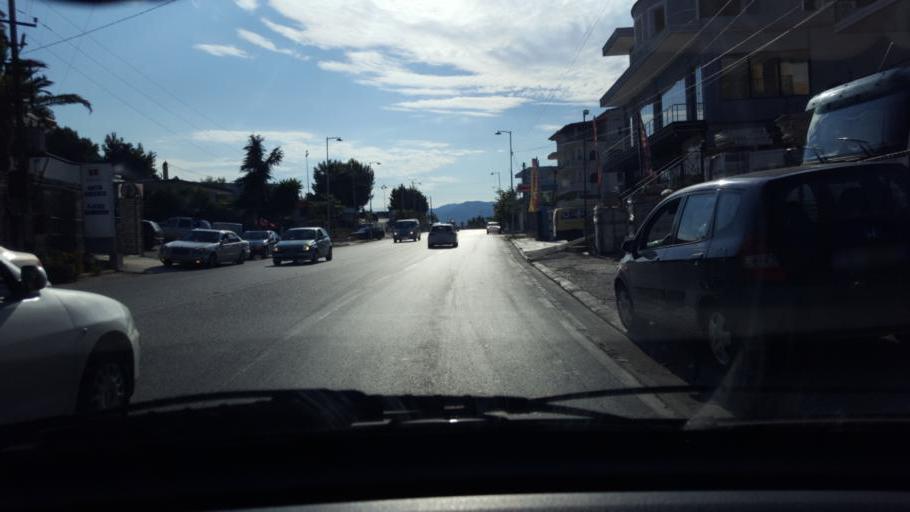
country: AL
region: Vlore
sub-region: Rrethi i Sarandes
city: Sarande
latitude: 39.8691
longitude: 20.0250
